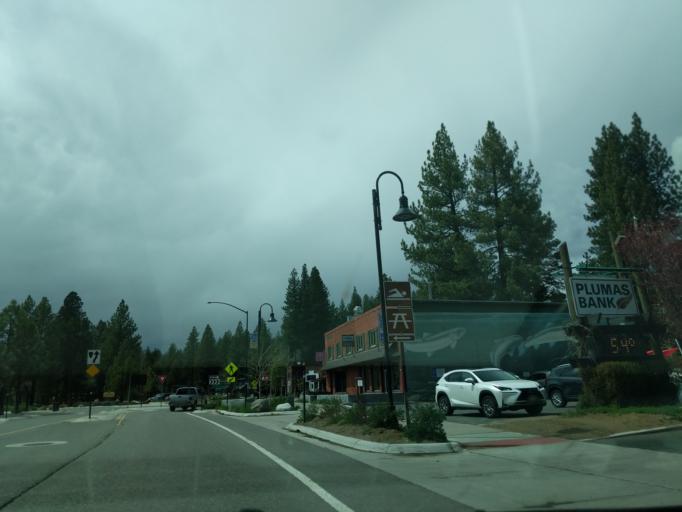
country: US
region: California
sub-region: Placer County
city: Kings Beach
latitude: 39.2365
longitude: -120.0240
